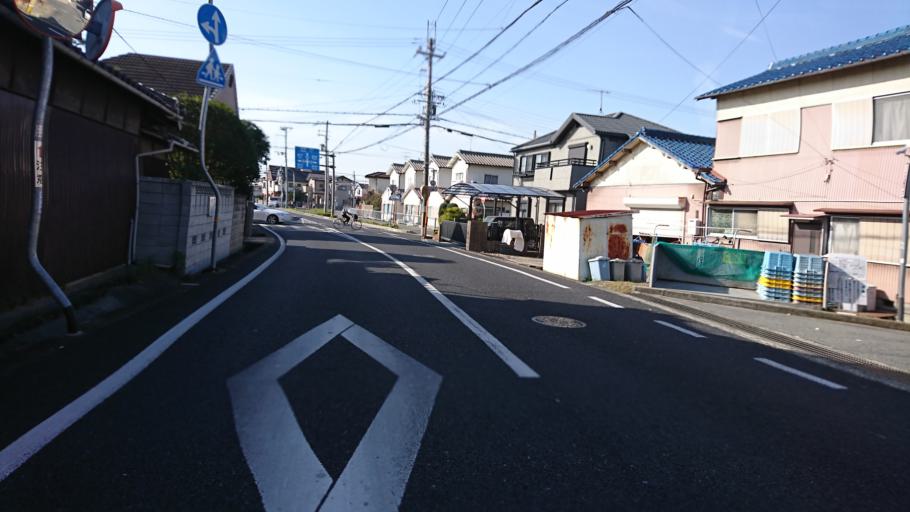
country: JP
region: Hyogo
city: Kakogawacho-honmachi
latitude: 34.7354
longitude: 134.8768
